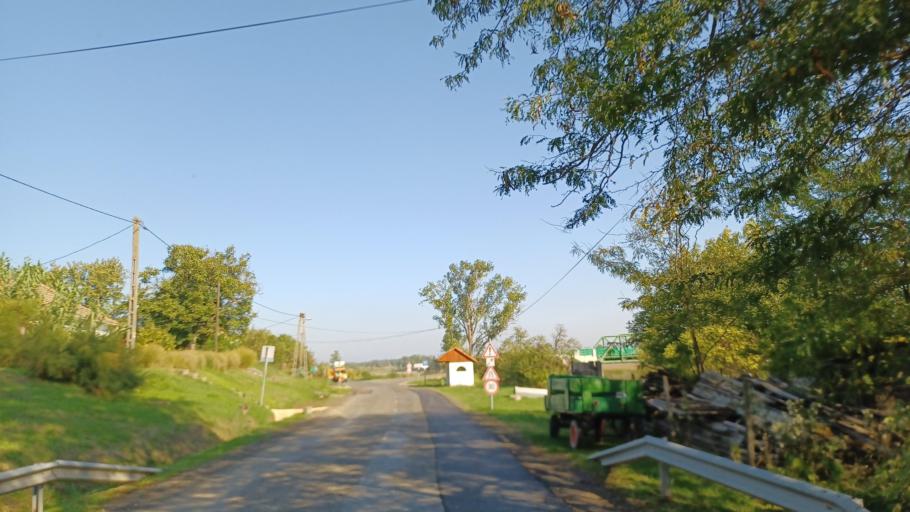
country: HU
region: Tolna
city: Nagydorog
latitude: 46.5609
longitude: 18.5916
